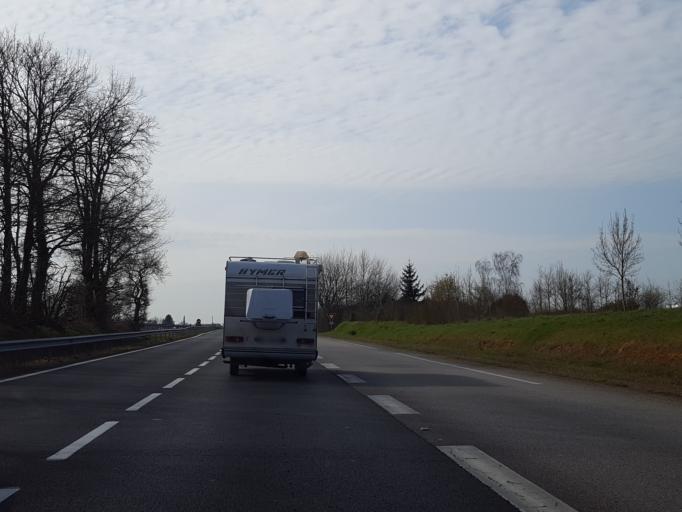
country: FR
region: Pays de la Loire
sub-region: Departement de la Vendee
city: Belleville-sur-Vie
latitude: 46.7566
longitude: -1.4308
